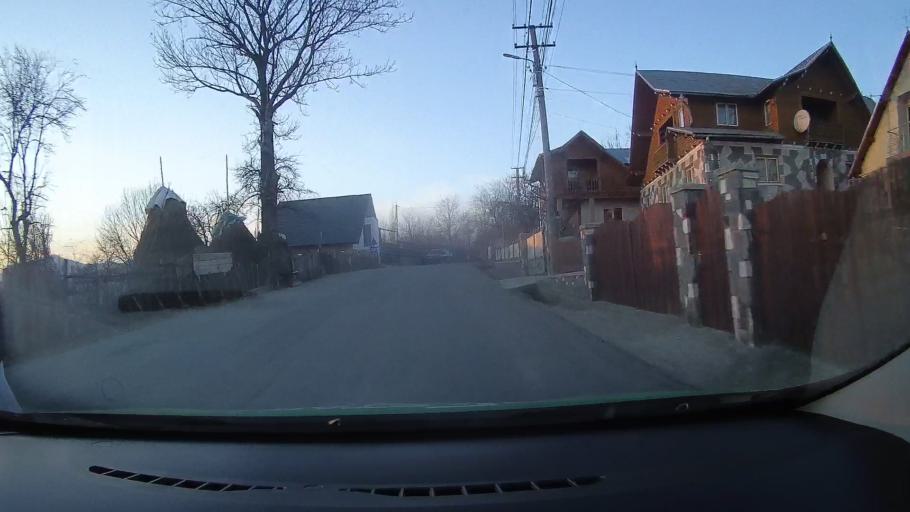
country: RO
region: Prahova
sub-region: Comuna Comarnic
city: Comarnic
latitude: 45.2538
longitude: 25.6437
